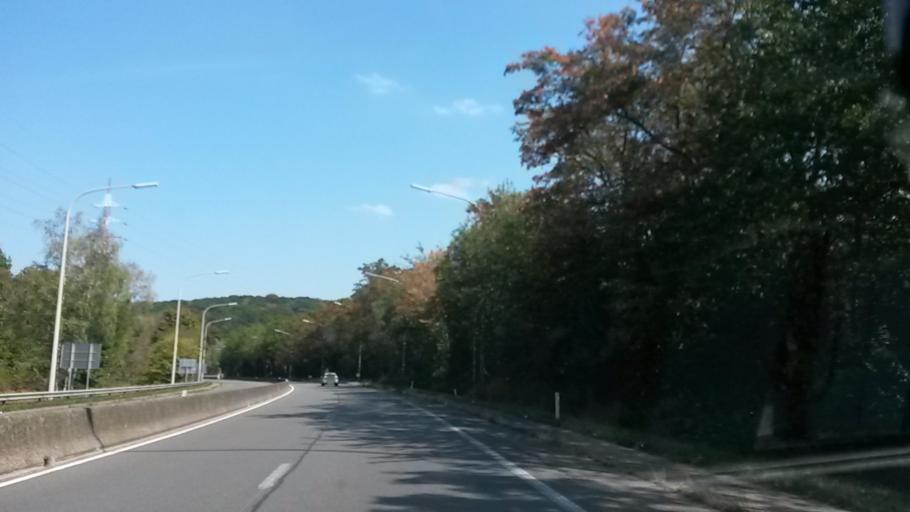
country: BE
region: Wallonia
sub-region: Province du Hainaut
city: Aiseau
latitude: 50.4522
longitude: 4.6085
